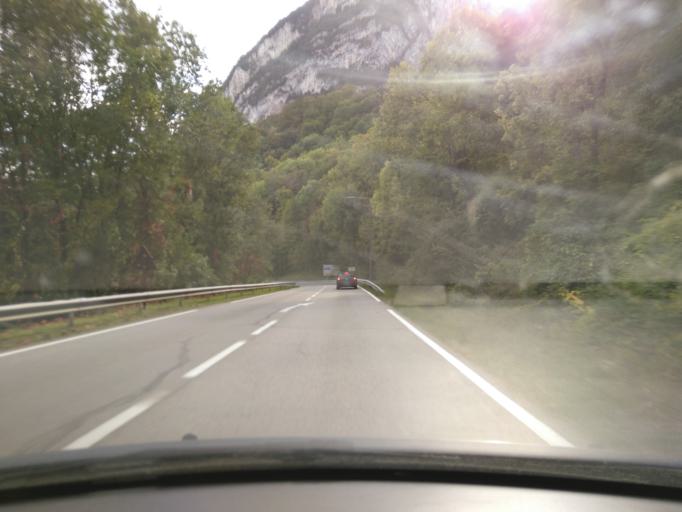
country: FR
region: Rhone-Alpes
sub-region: Departement de l'Isere
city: Sassenage
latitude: 45.2136
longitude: 5.6551
